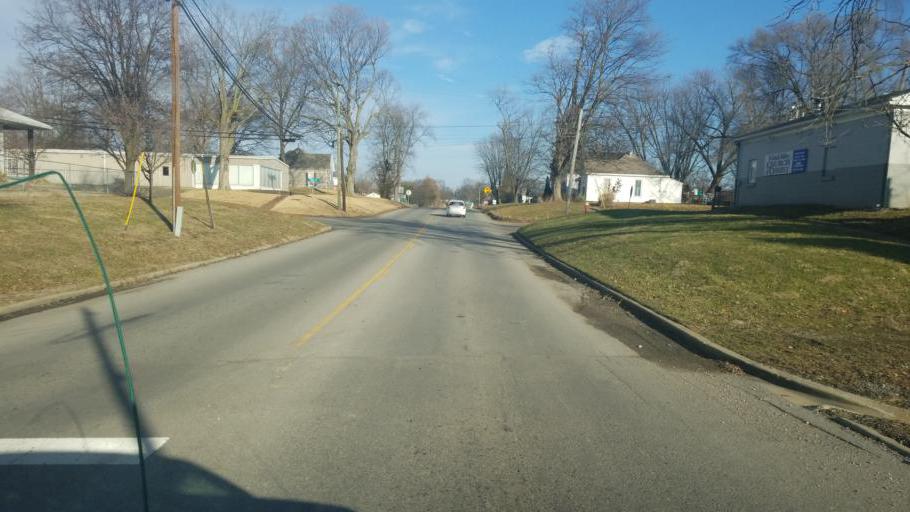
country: US
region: Illinois
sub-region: Wabash County
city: Mount Carmel
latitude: 38.4058
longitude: -87.7671
